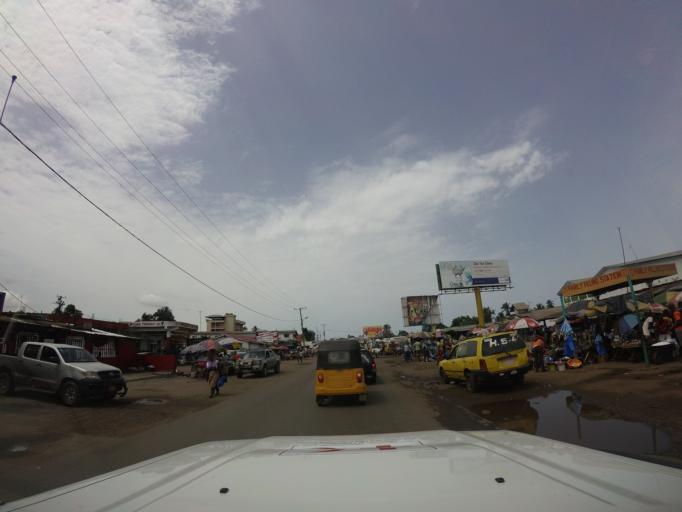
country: LR
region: Montserrado
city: Monrovia
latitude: 6.3758
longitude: -10.7857
